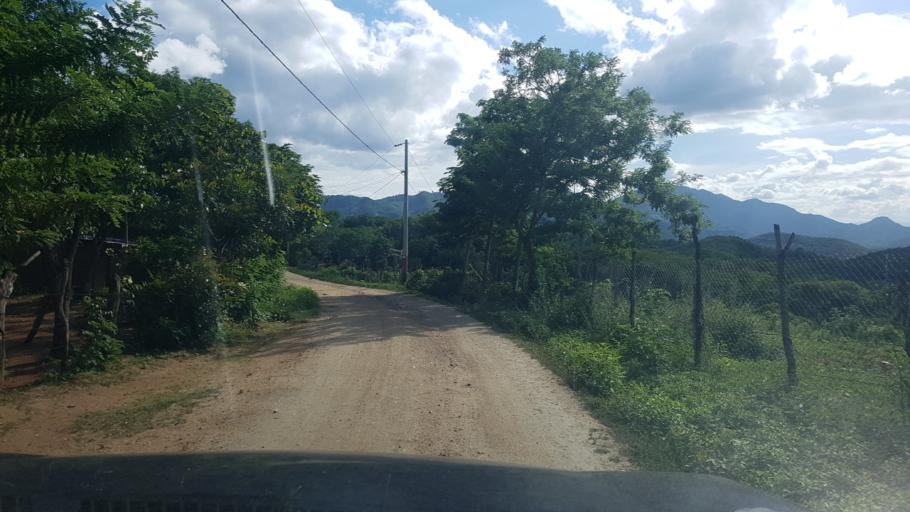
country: NI
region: Nueva Segovia
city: Mozonte
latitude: 13.6505
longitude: -86.3985
